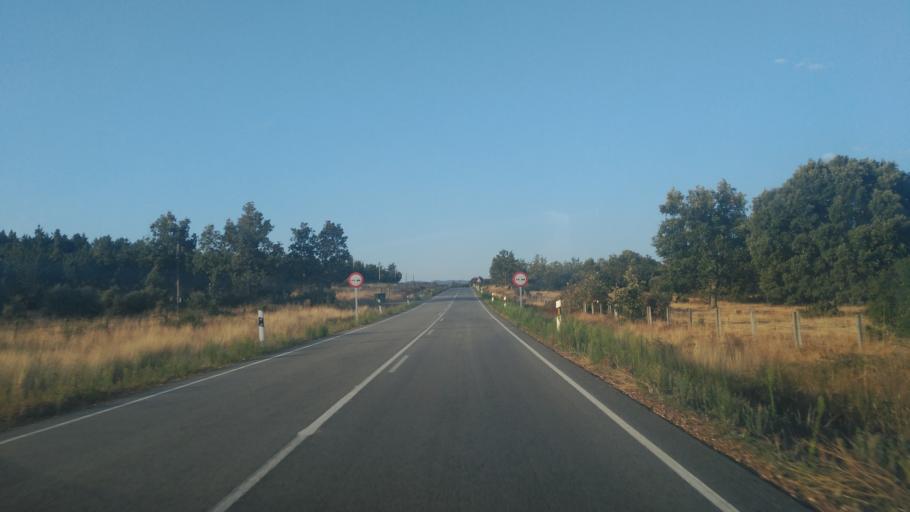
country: ES
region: Castille and Leon
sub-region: Provincia de Salamanca
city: Puebla de Yeltes
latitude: 40.6253
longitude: -6.1408
